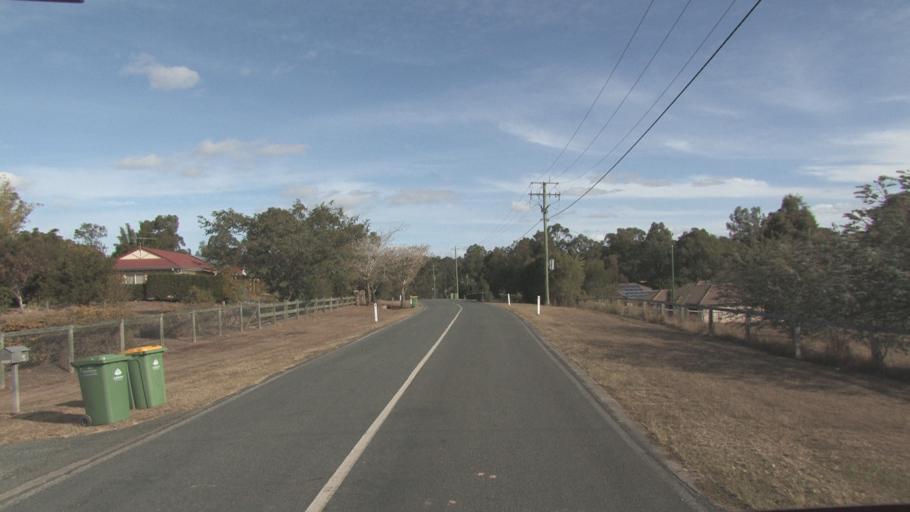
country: AU
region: Queensland
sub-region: Logan
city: Cedar Vale
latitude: -27.8744
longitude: 153.0031
